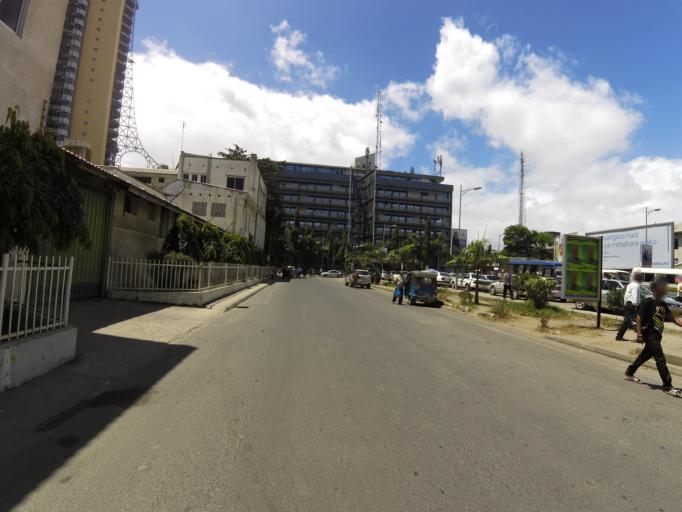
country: TZ
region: Dar es Salaam
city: Dar es Salaam
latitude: -6.8216
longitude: 39.2852
